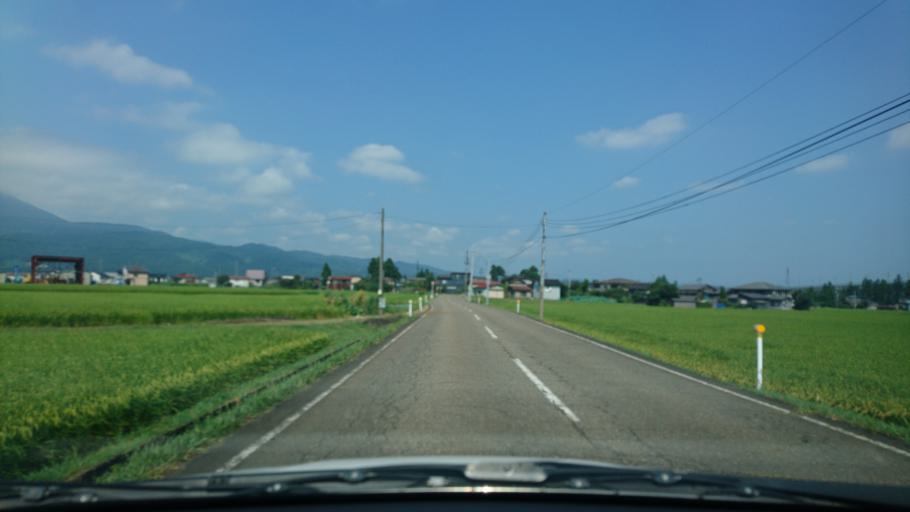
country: JP
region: Niigata
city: Arai
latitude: 37.0660
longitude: 138.2619
